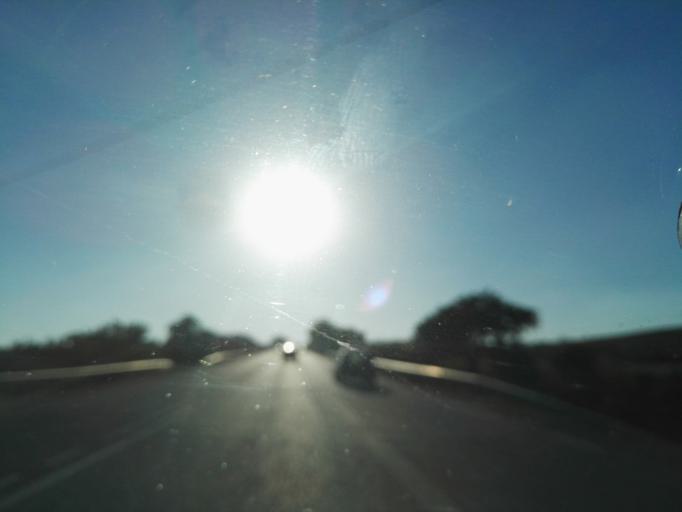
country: PT
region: Evora
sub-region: Borba
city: Borba
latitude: 38.8190
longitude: -7.4381
